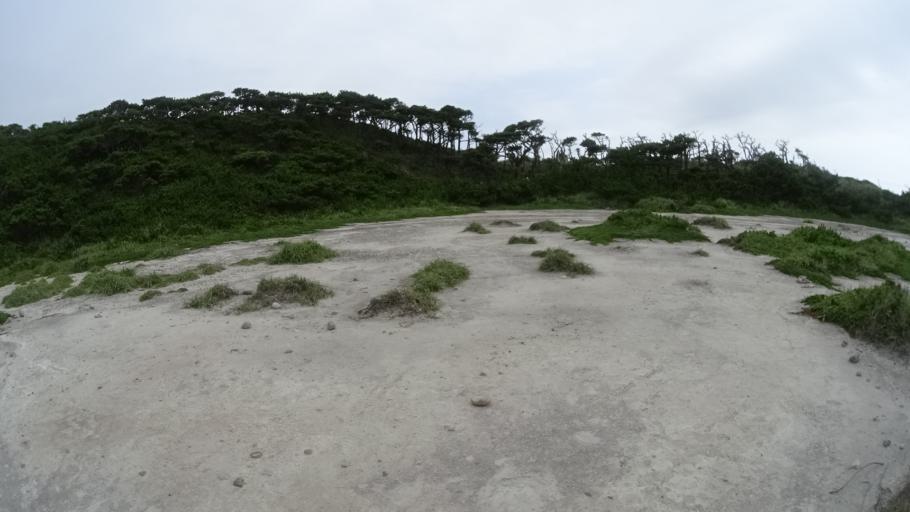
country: JP
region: Shizuoka
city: Shimoda
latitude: 34.3178
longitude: 139.1990
